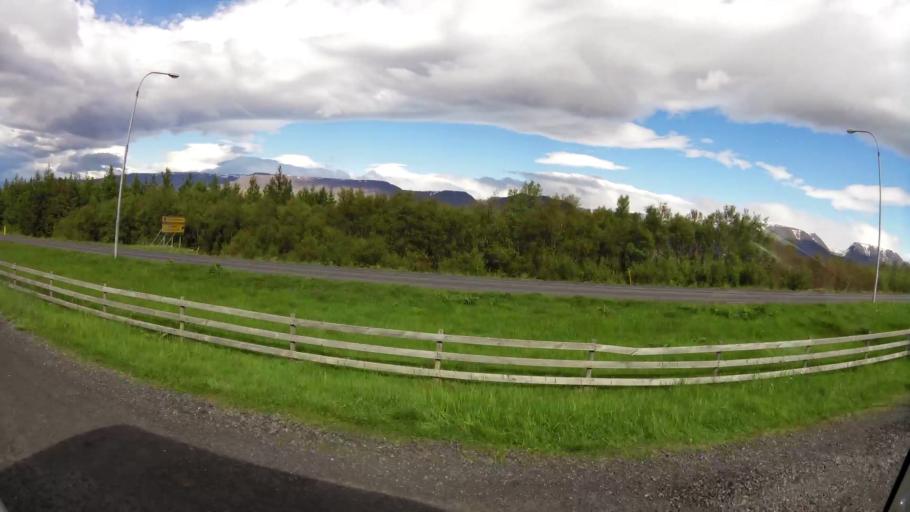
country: IS
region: Northwest
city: Saudarkrokur
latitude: 65.5511
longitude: -19.4438
